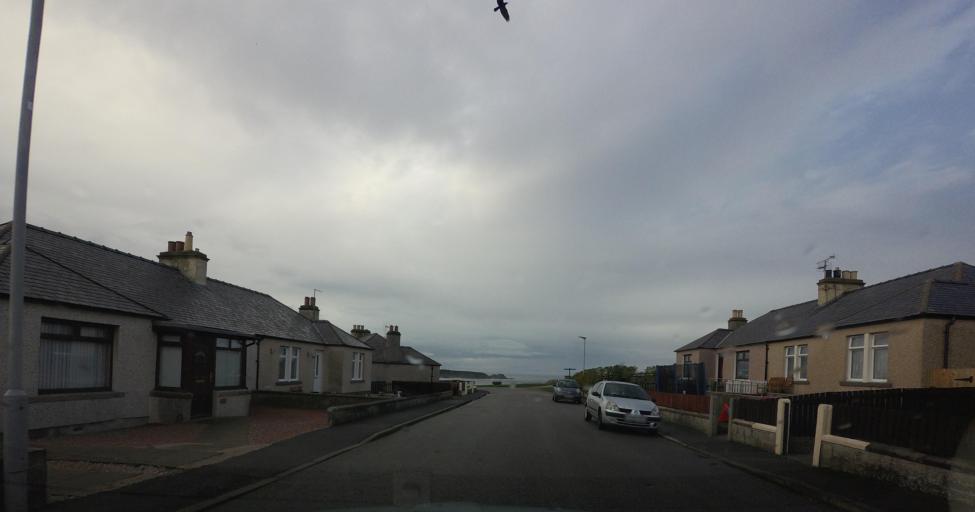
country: GB
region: Scotland
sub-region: Moray
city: Cullen
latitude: 57.6931
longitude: -2.8159
